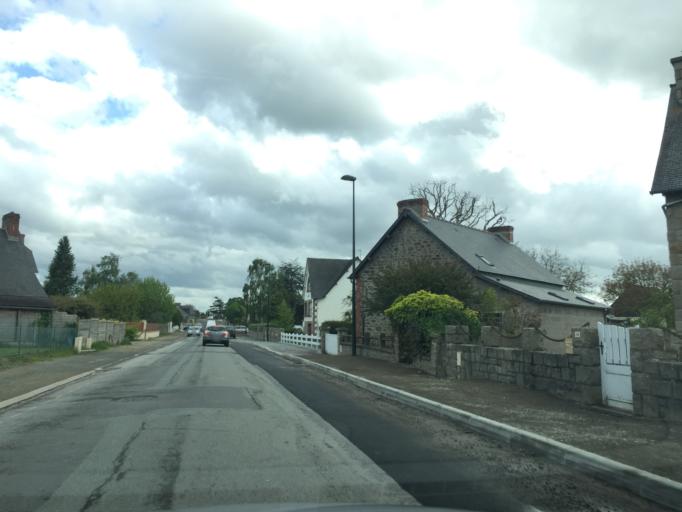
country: FR
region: Brittany
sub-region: Departement des Cotes-d'Armor
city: Ploubalay
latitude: 48.5840
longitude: -2.1432
